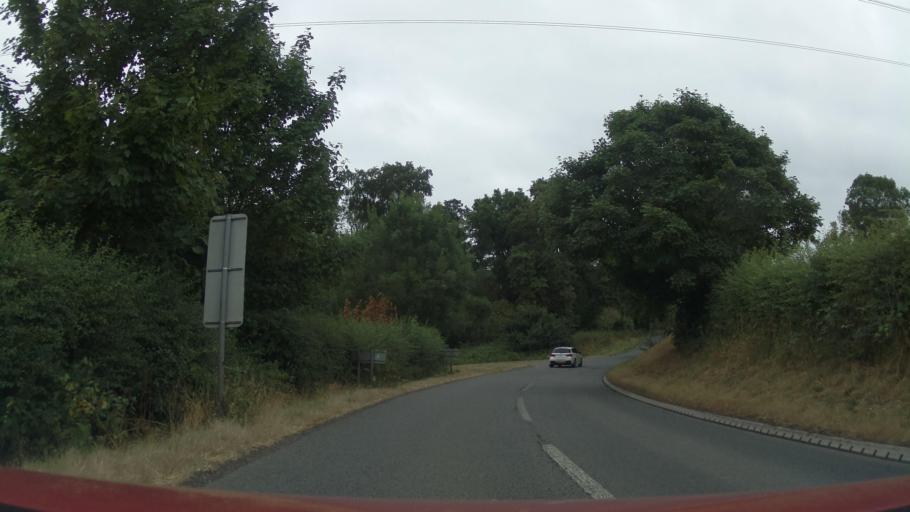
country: GB
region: England
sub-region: Derbyshire
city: Repton
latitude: 52.8244
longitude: -1.5378
